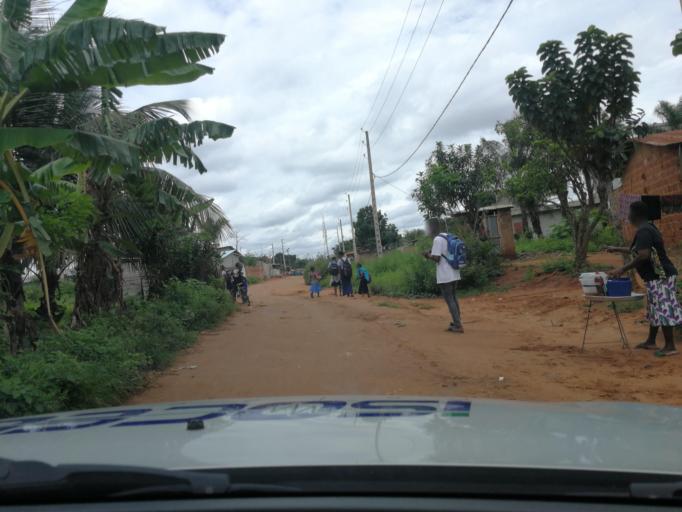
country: BJ
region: Atlantique
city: Abomey-Calavi
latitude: 6.4349
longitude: 2.3063
